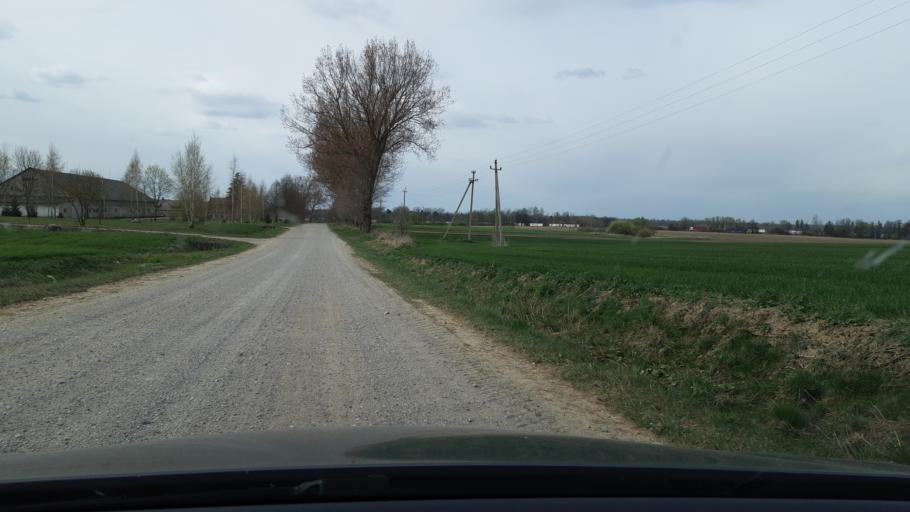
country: LT
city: Virbalis
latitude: 54.6183
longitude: 22.8403
